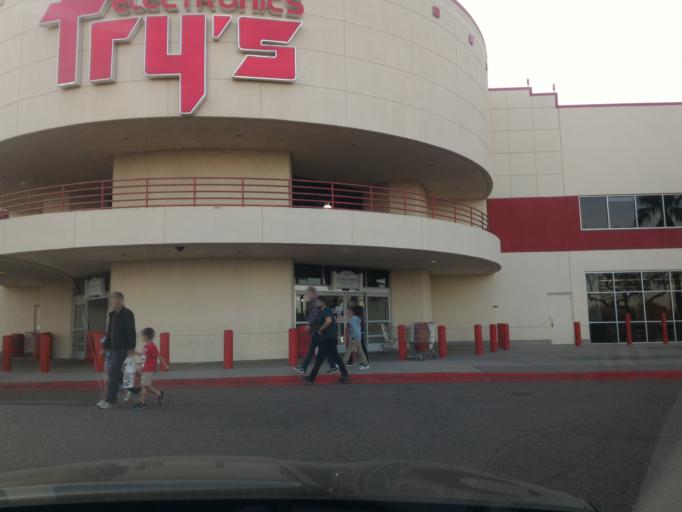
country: US
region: Arizona
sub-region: Maricopa County
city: Guadalupe
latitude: 33.3790
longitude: -111.9719
